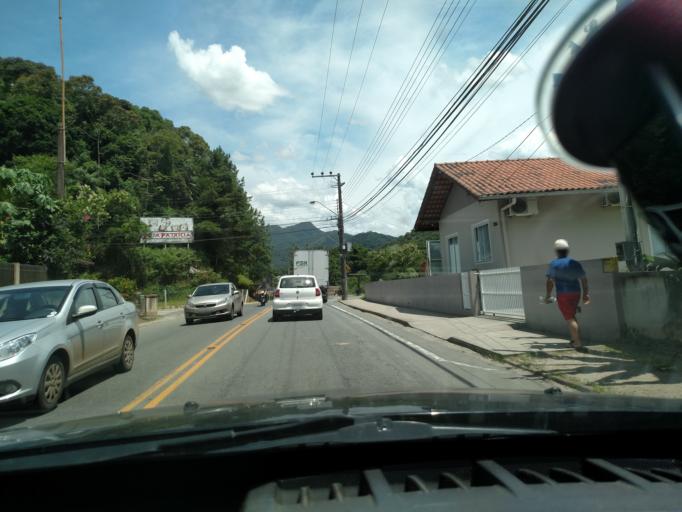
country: BR
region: Santa Catarina
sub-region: Blumenau
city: Blumenau
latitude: -26.9725
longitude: -49.0767
